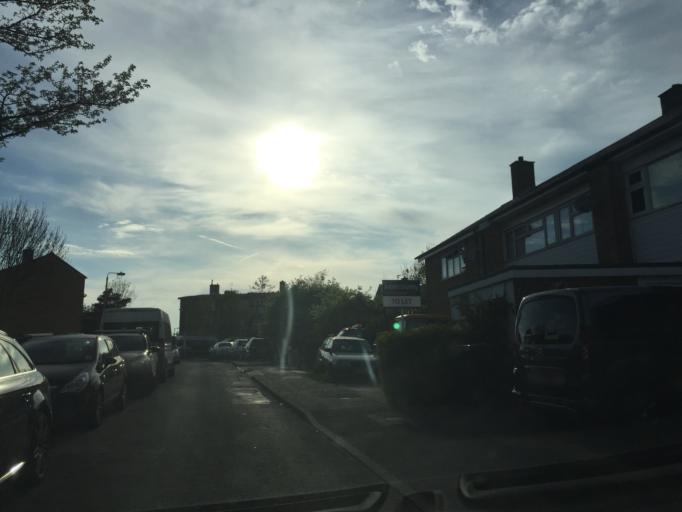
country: GB
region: England
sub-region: Essex
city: Harlow
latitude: 51.7583
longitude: 0.1230
